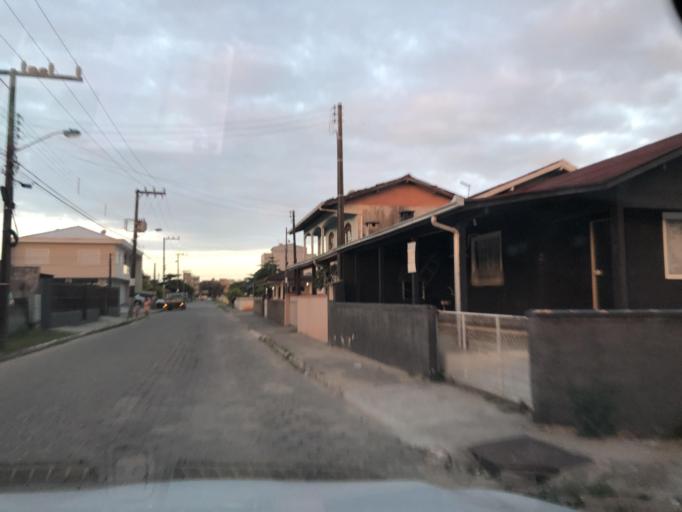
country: BR
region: Santa Catarina
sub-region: Sao Francisco Do Sul
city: Sao Francisco do Sul
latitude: -26.2305
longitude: -48.5088
